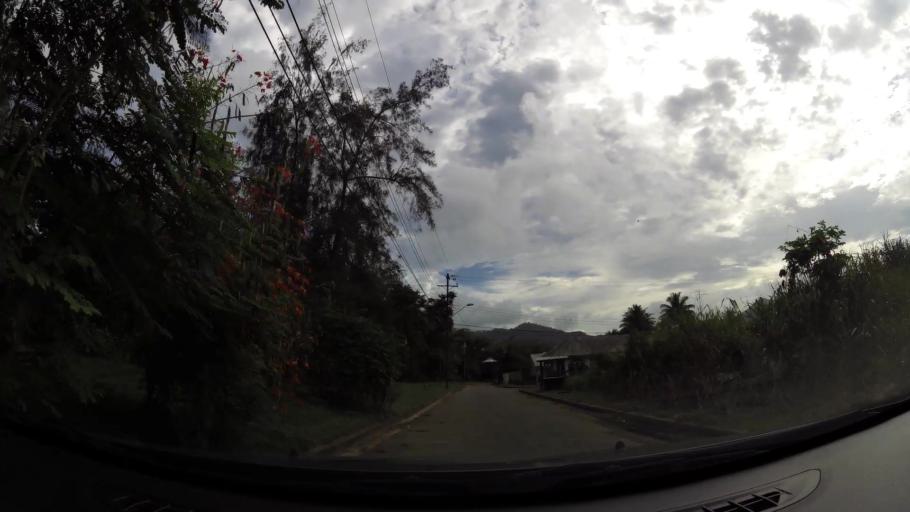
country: TT
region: Diego Martin
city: Petit Valley
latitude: 10.7148
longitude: -61.4806
